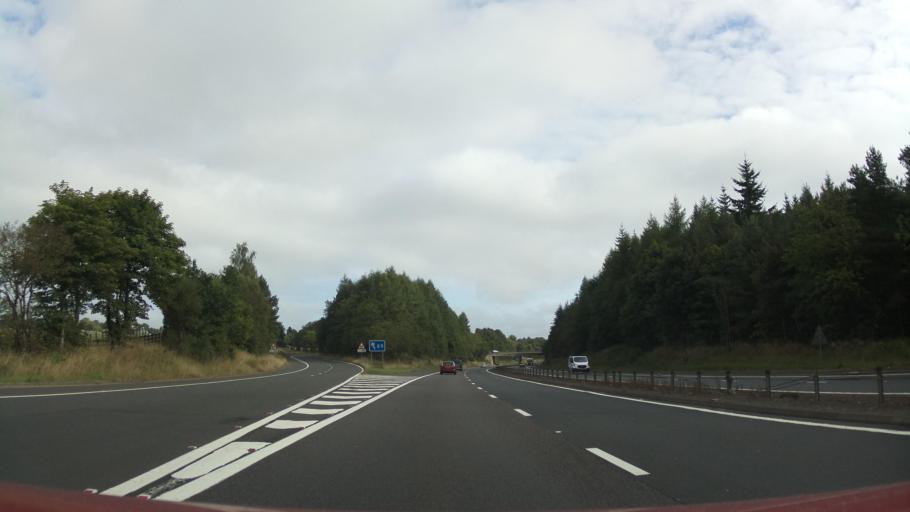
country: GB
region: Scotland
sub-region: Falkirk
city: Larbert
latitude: 56.0278
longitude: -3.8591
